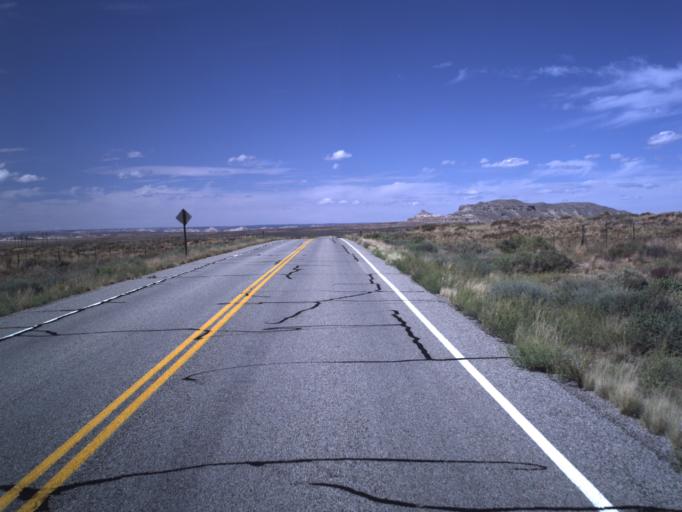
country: US
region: Utah
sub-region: San Juan County
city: Blanding
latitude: 37.2996
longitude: -109.4335
